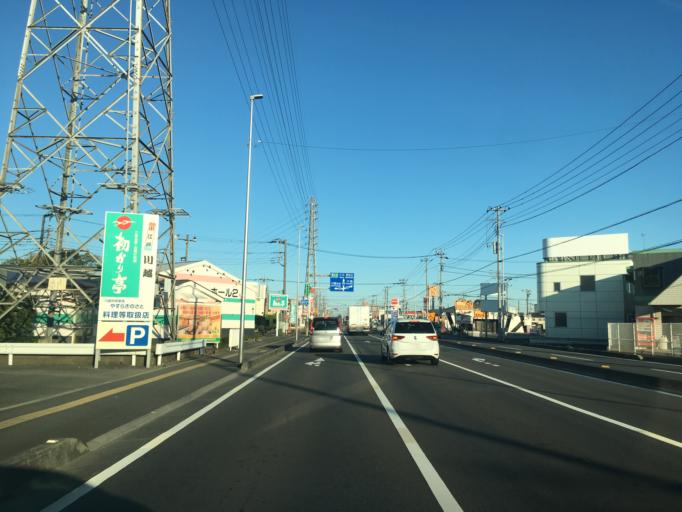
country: JP
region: Saitama
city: Kawagoe
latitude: 35.9339
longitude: 139.4872
